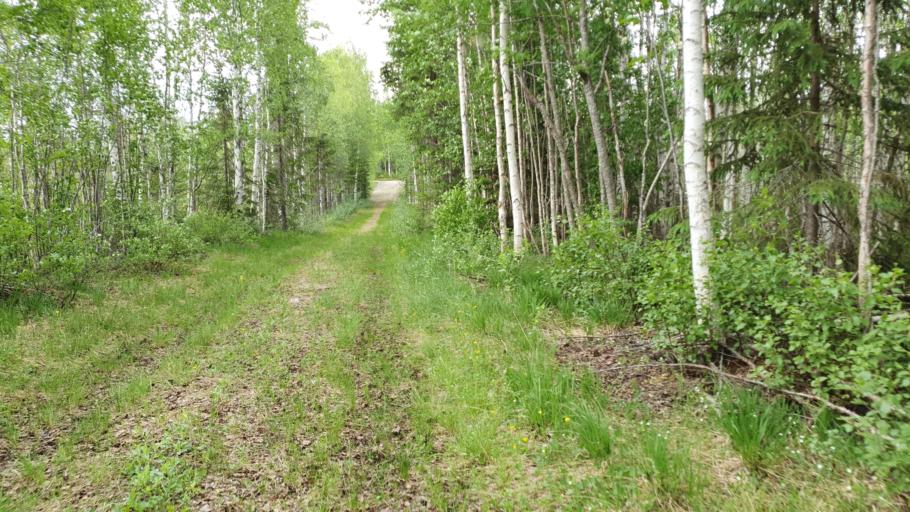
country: FI
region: Kainuu
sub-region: Kehys-Kainuu
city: Kuhmo
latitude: 64.4505
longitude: 29.6663
